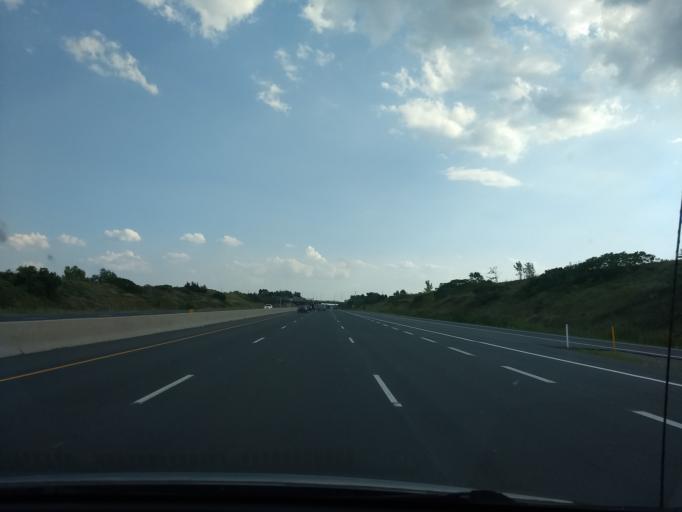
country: CA
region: Ontario
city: Burlington
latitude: 43.3787
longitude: -79.8331
